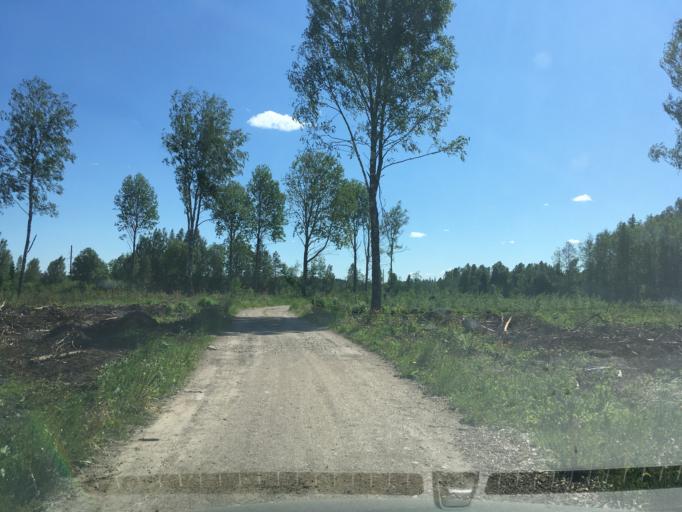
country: EE
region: Harju
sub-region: Raasiku vald
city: Raasiku
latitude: 59.1548
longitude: 25.1446
